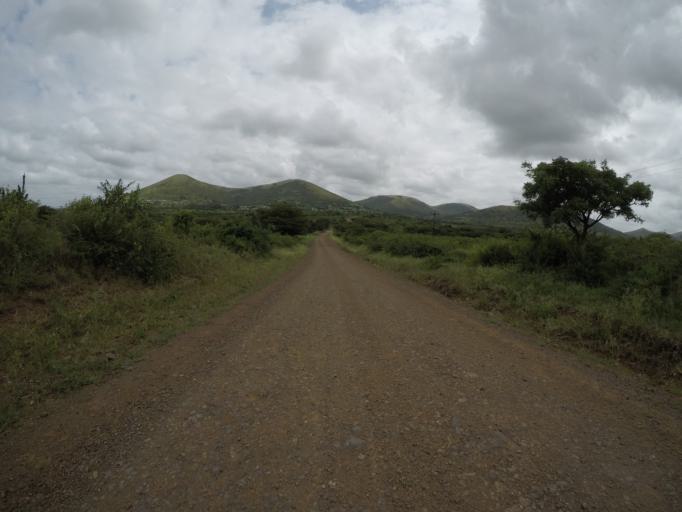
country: ZA
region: KwaZulu-Natal
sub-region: uThungulu District Municipality
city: Empangeni
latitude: -28.5980
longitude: 31.8926
